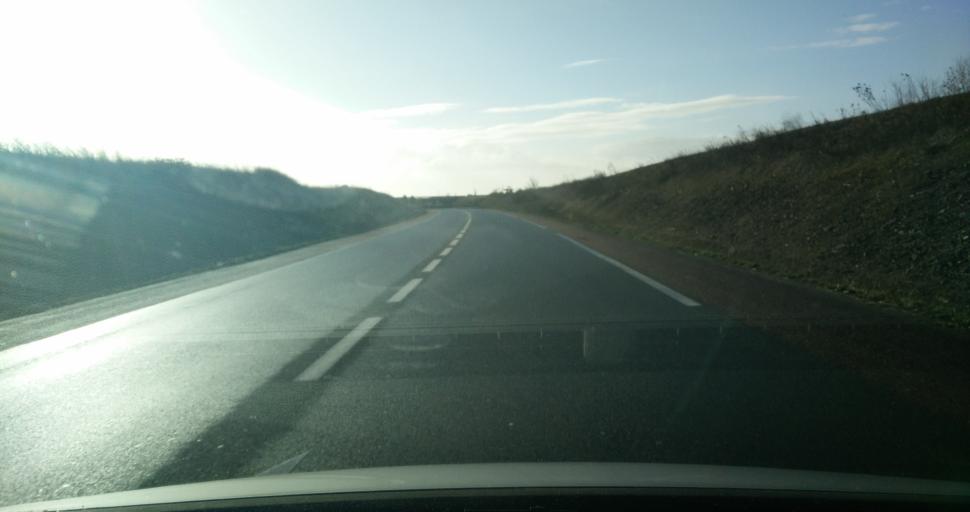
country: FR
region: Poitou-Charentes
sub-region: Departement de la Charente-Maritime
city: Saint-Xandre
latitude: 46.1840
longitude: -1.0928
